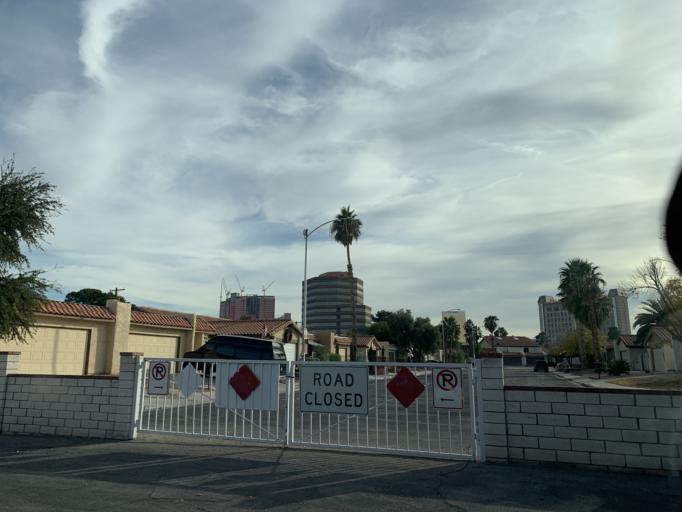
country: US
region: Nevada
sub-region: Clark County
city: Las Vegas
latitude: 36.1477
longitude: -115.1748
